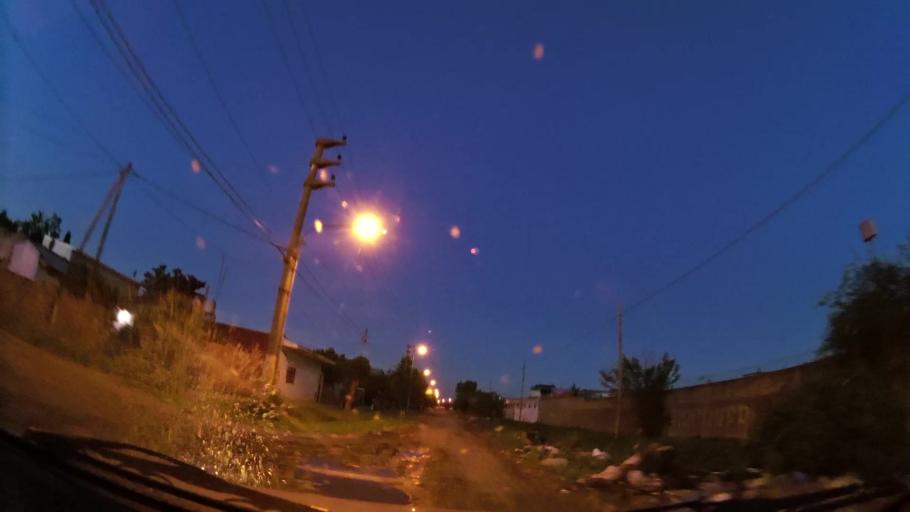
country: AR
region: Buenos Aires
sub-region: Partido de Almirante Brown
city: Adrogue
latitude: -34.7526
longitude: -58.3343
